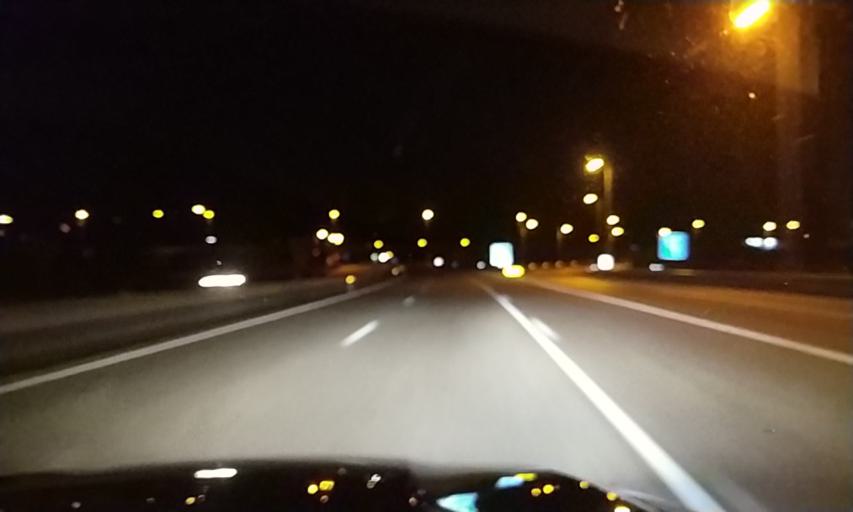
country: PT
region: Santarem
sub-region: Alcanena
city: Alcanena
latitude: 39.4749
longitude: -8.6298
